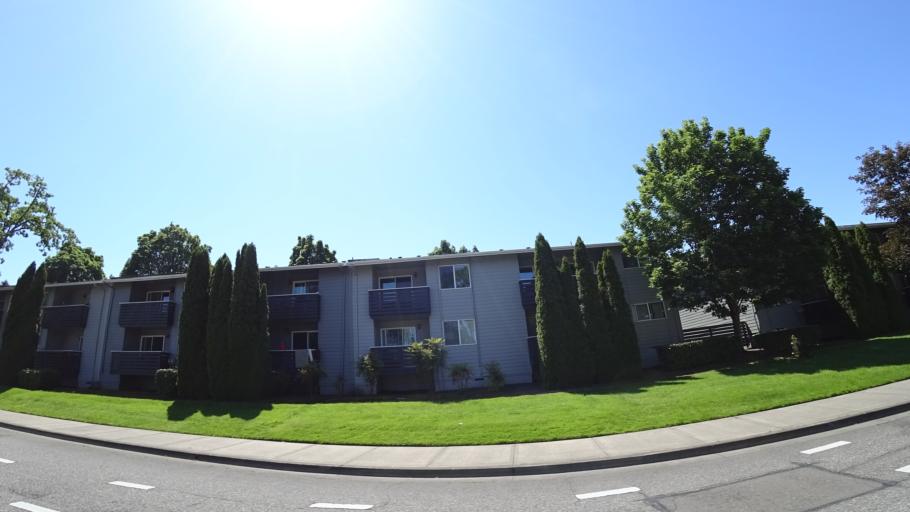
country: US
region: Oregon
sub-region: Washington County
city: Beaverton
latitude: 45.4921
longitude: -122.8170
